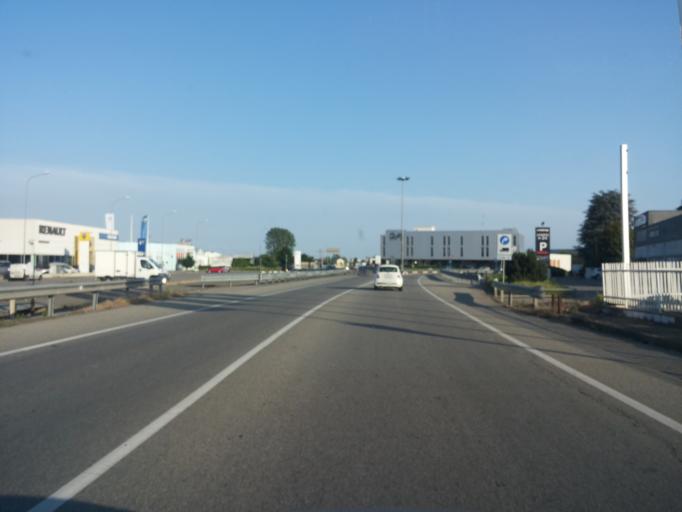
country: IT
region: Piedmont
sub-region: Provincia di Vercelli
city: Caresanablot
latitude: 45.3491
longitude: 8.3958
